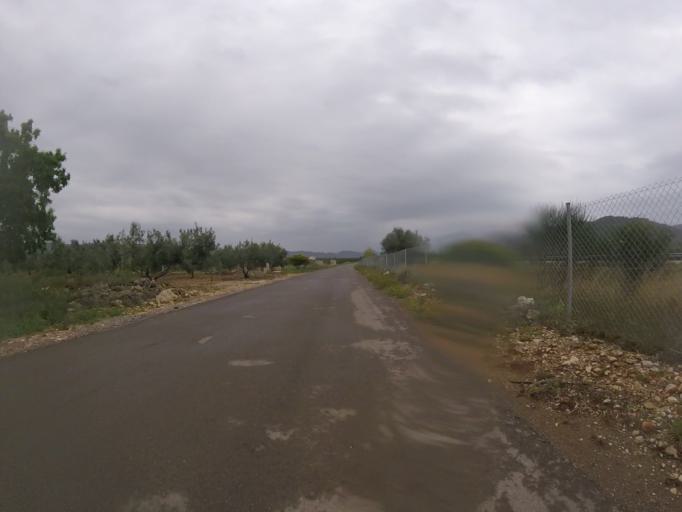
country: ES
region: Valencia
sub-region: Provincia de Castello
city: Alcala de Xivert
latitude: 40.2907
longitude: 0.2289
